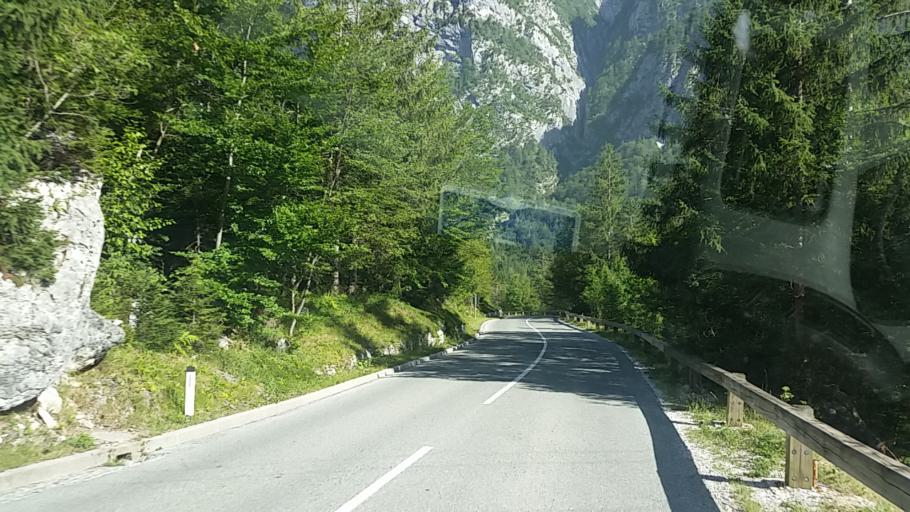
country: SI
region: Kranjska Gora
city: Kranjska Gora
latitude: 46.3850
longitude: 13.7526
